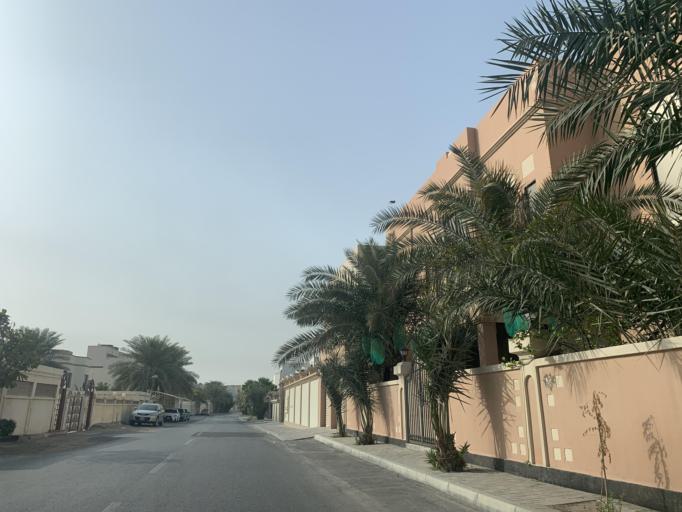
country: BH
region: Northern
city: Madinat `Isa
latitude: 26.1944
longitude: 50.5596
